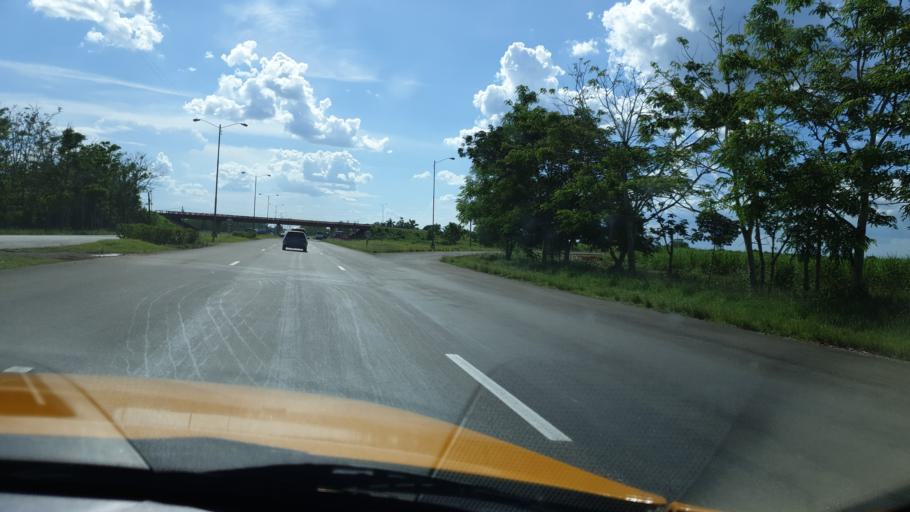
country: CU
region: Cienfuegos
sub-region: Municipio de Aguada de Pasajeros
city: Aguada de Pasajeros
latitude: 22.4032
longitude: -80.8603
